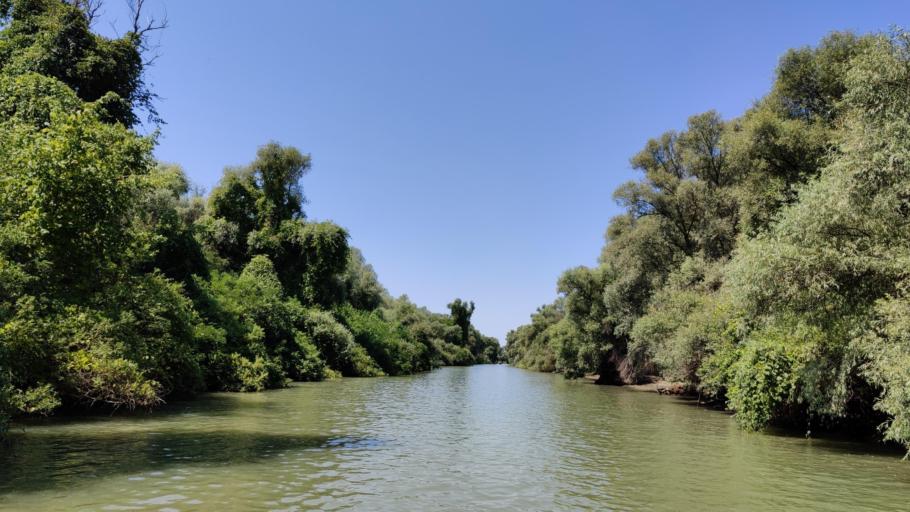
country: RO
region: Tulcea
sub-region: Comuna Pardina
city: Pardina
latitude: 45.2533
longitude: 28.9497
